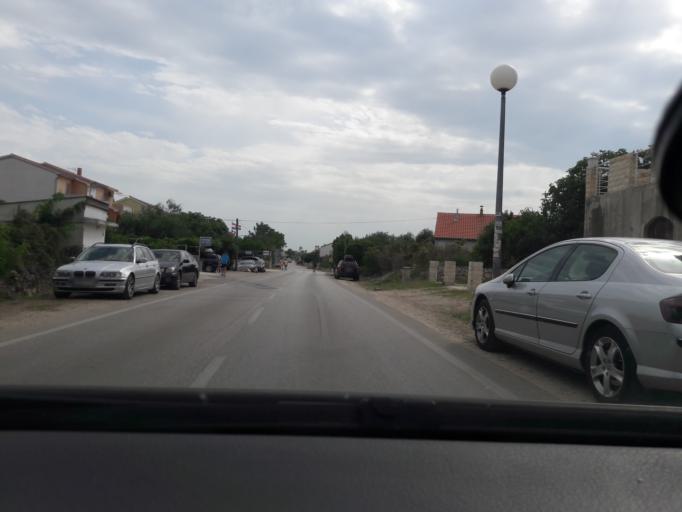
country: HR
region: Zadarska
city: Vir
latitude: 44.3003
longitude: 15.0791
